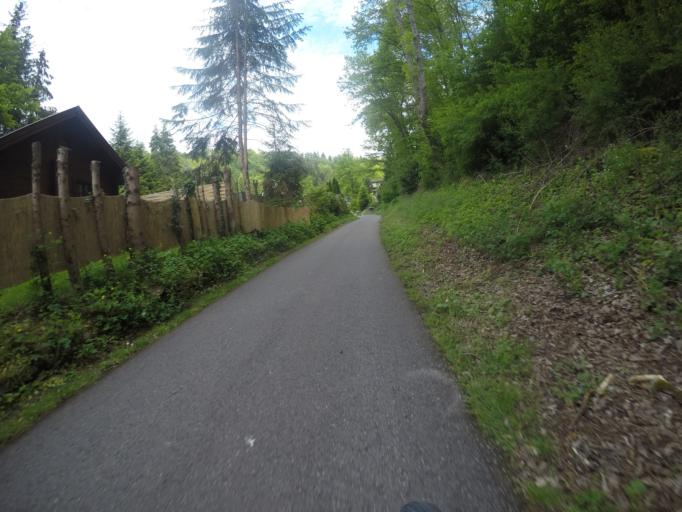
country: DE
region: Baden-Wuerttemberg
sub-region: Karlsruhe Region
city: Wildberg
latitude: 48.6107
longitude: 8.7356
